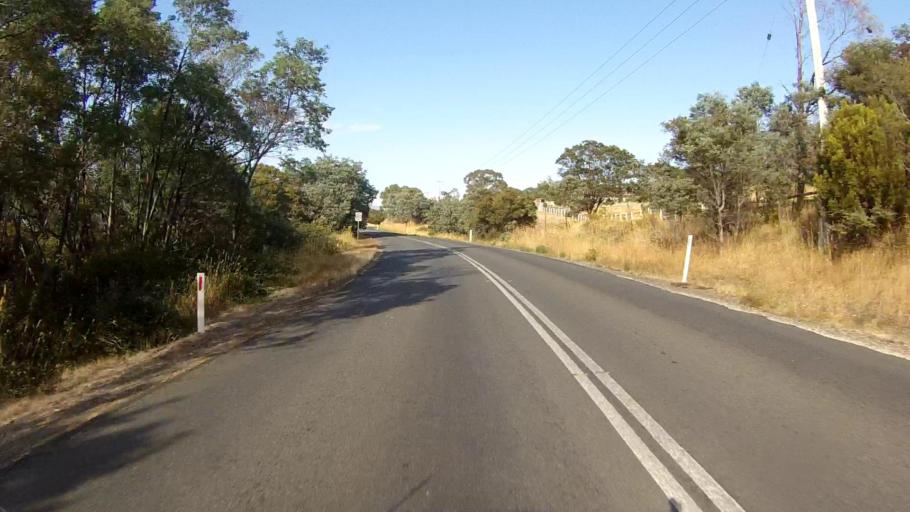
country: AU
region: Tasmania
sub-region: Glenorchy
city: Granton
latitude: -42.7554
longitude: 147.1436
